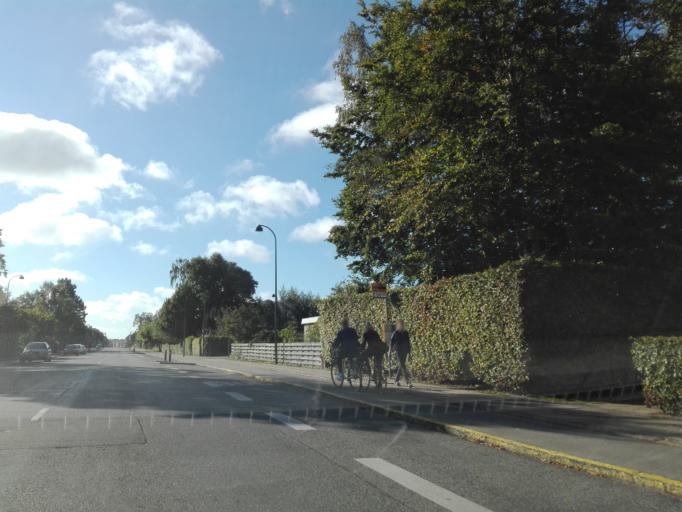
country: DK
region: Capital Region
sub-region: Lyngby-Tarbaek Kommune
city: Kongens Lyngby
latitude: 55.7368
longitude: 12.5240
